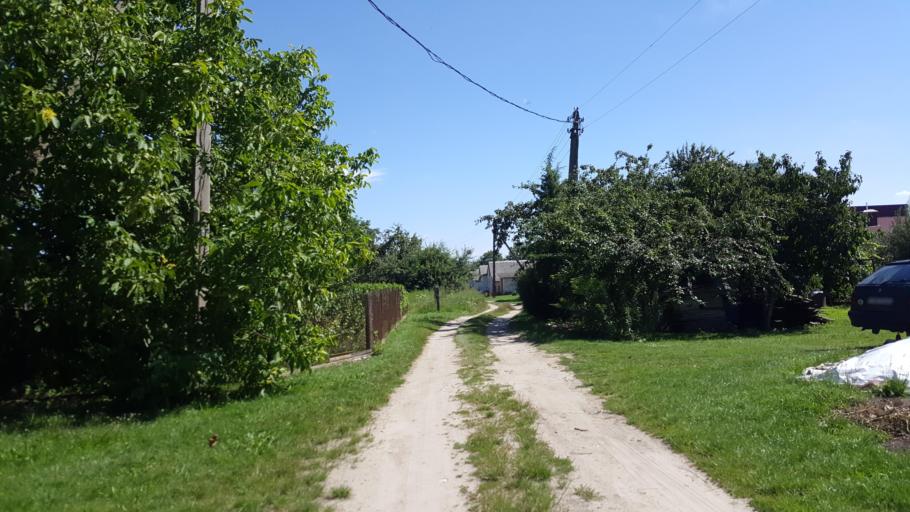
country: BY
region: Brest
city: Charnawchytsy
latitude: 52.2650
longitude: 23.5887
